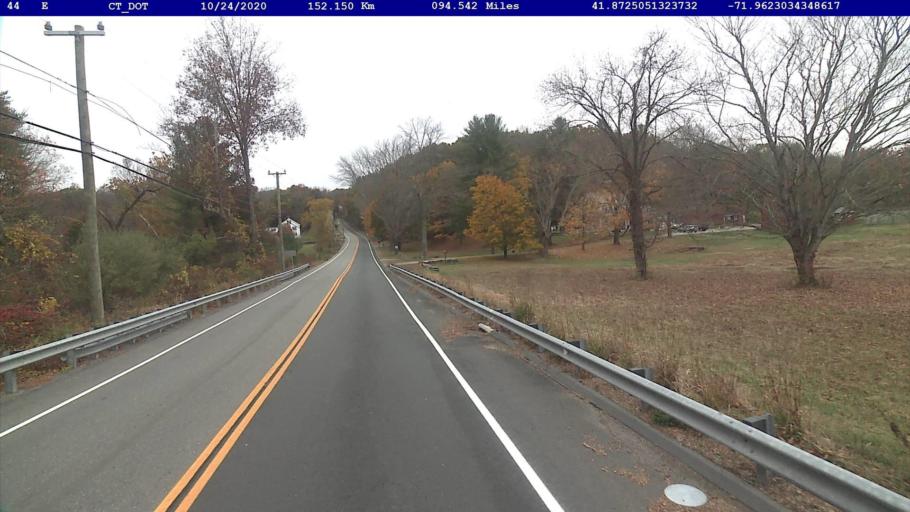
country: US
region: Connecticut
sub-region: Windham County
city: South Woodstock
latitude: 41.8725
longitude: -71.9622
